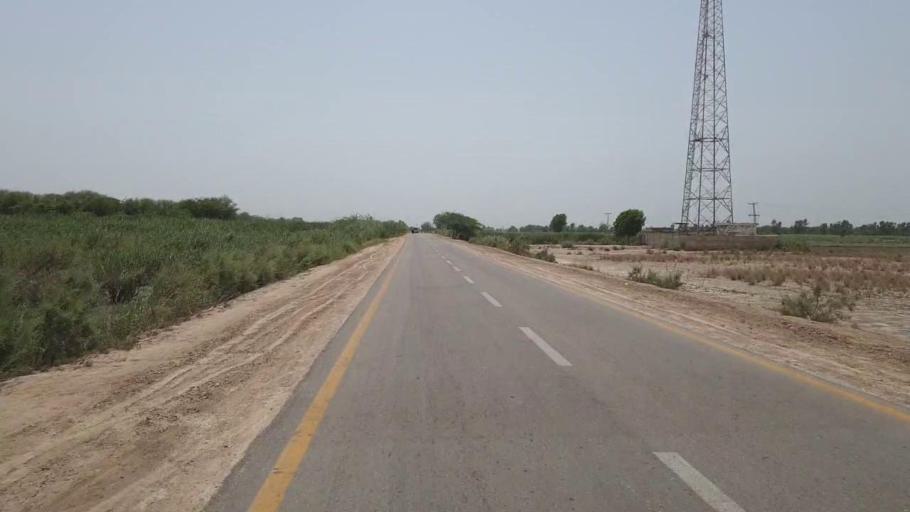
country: PK
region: Sindh
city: Moro
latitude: 26.6021
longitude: 68.0647
